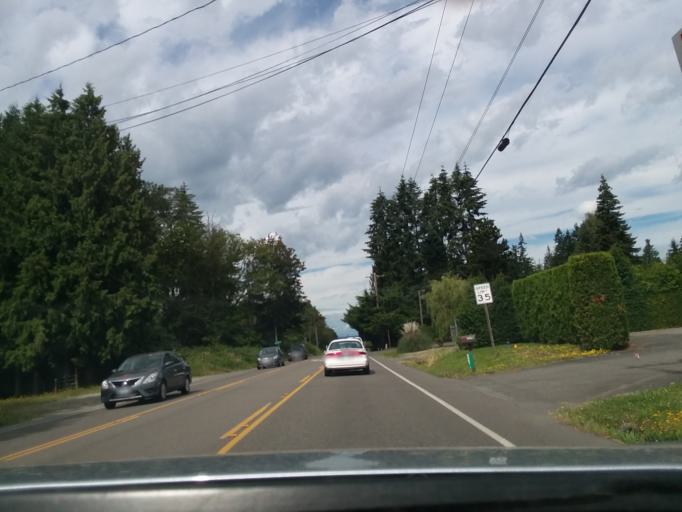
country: US
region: Washington
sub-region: Snohomish County
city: West Lake Stevens
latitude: 47.9781
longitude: -122.1149
